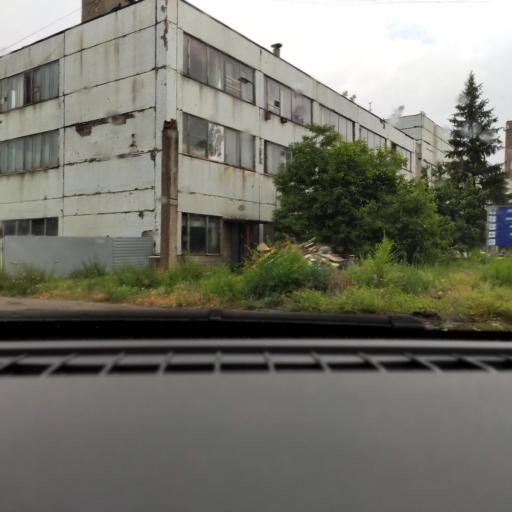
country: RU
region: Voronezj
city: Somovo
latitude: 51.7159
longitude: 39.2884
